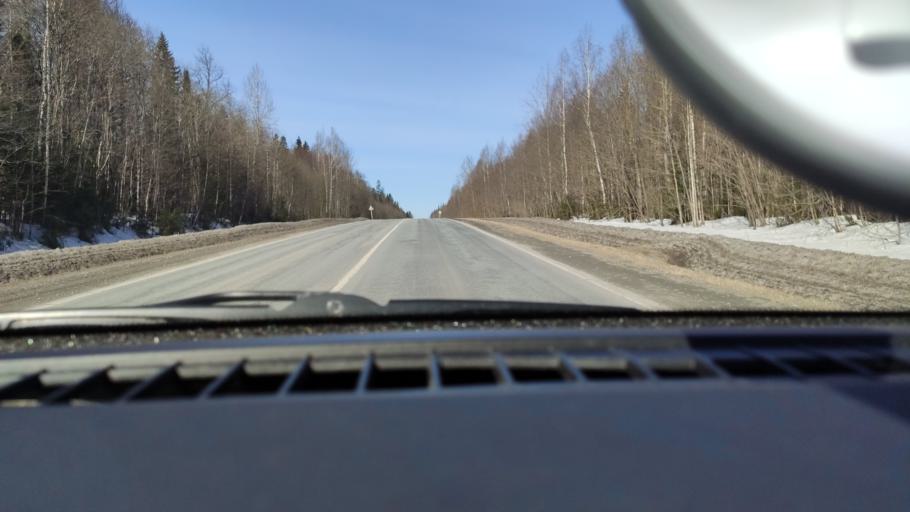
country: RU
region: Perm
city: Perm
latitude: 58.1787
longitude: 56.2269
